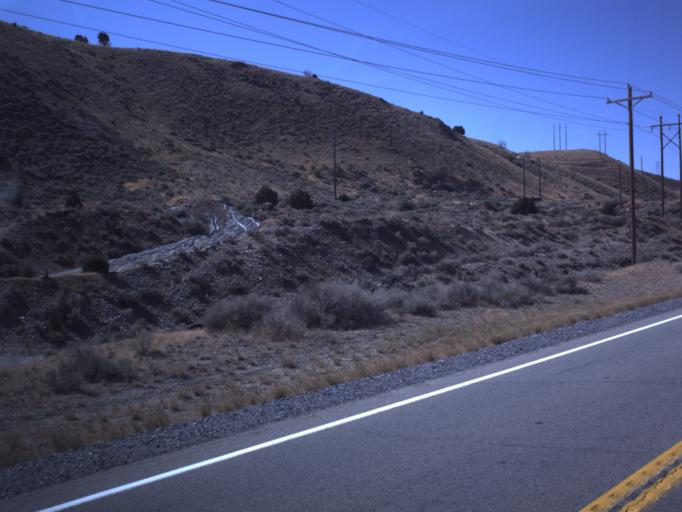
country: US
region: Utah
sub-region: Tooele County
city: Tooele
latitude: 40.4800
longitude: -112.3446
